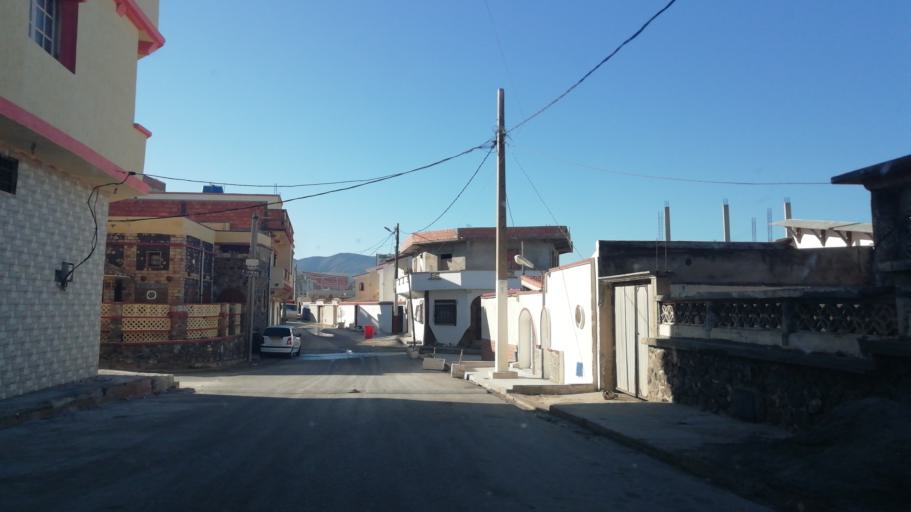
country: DZ
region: Oran
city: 'Ain el Turk
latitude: 35.7254
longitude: -0.8489
